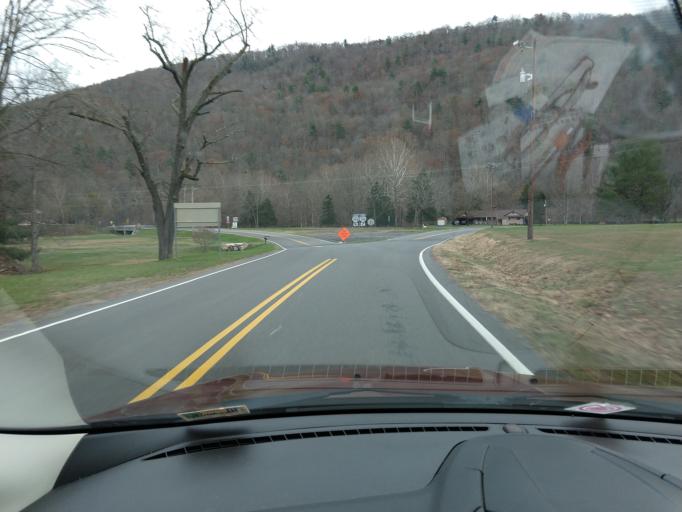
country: US
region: West Virginia
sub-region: Greenbrier County
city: White Sulphur Springs
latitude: 37.7194
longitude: -80.2029
